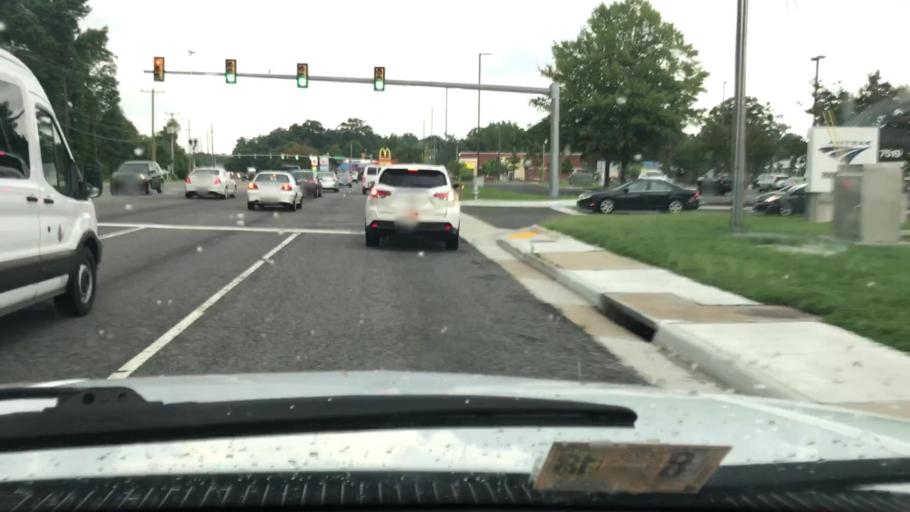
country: US
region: Virginia
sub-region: Henrico County
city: Dumbarton
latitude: 37.6168
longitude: -77.4983
